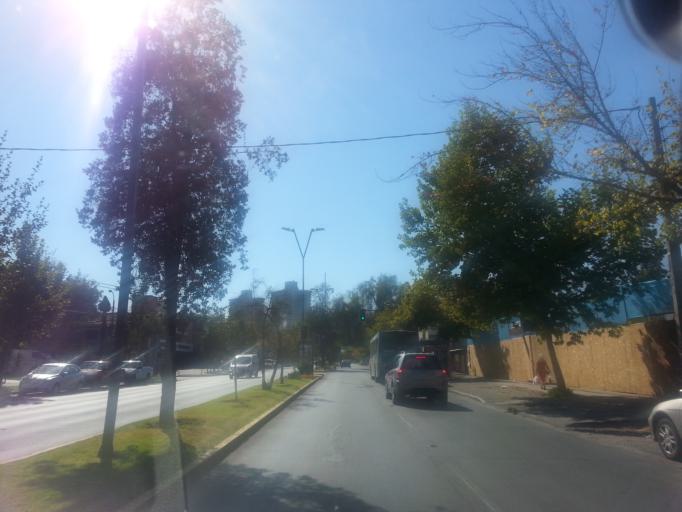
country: CL
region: Santiago Metropolitan
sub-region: Provincia de Santiago
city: Villa Presidente Frei, Nunoa, Santiago, Chile
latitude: -33.4357
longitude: -70.5923
